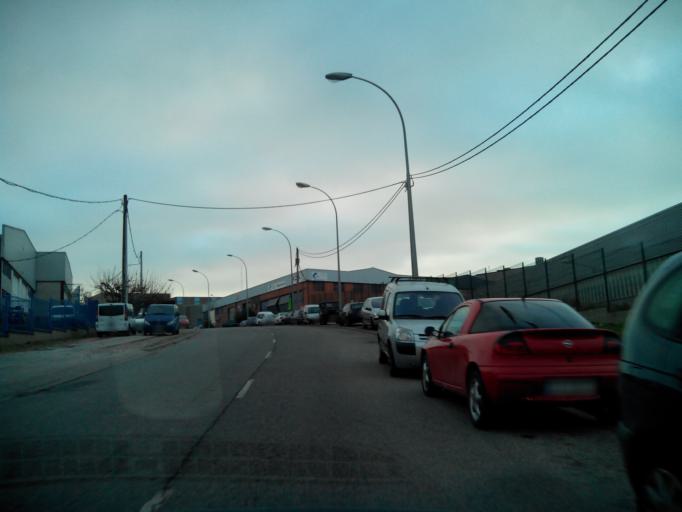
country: ES
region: Catalonia
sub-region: Provincia de Barcelona
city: Manresa
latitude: 41.7126
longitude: 1.8457
